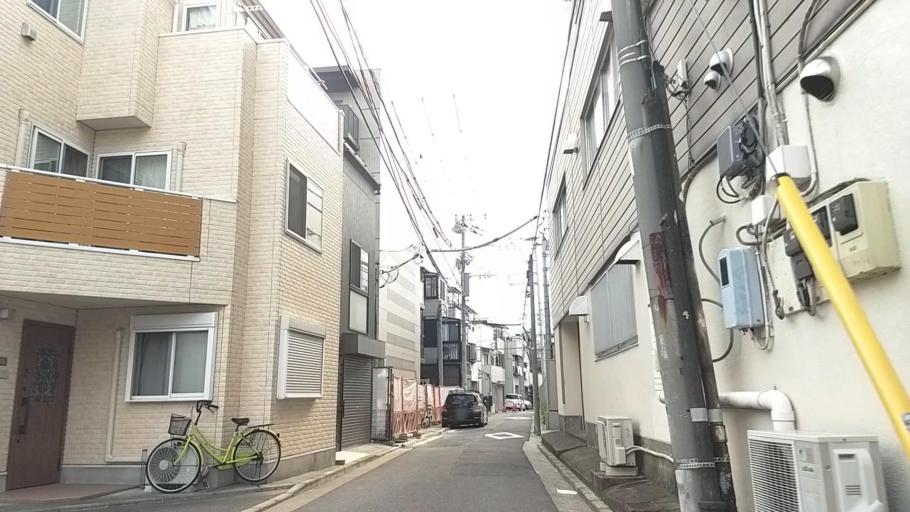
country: JP
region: Kanagawa
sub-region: Kawasaki-shi
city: Kawasaki
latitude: 35.5032
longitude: 139.6812
